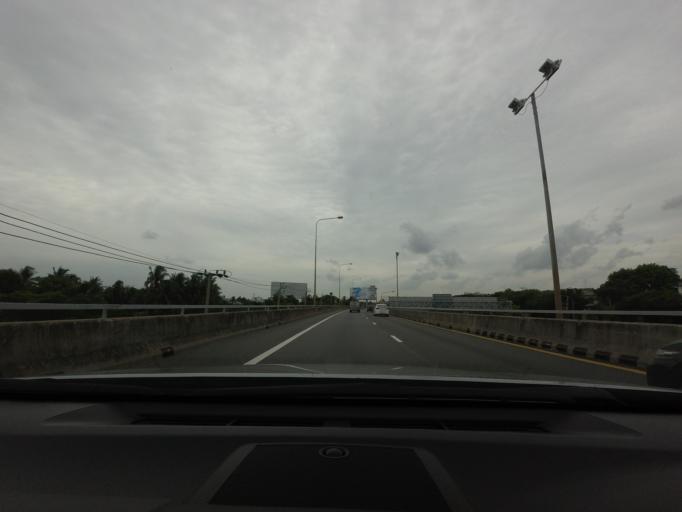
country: TH
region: Bangkok
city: Chom Thong
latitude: 13.6754
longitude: 100.4811
